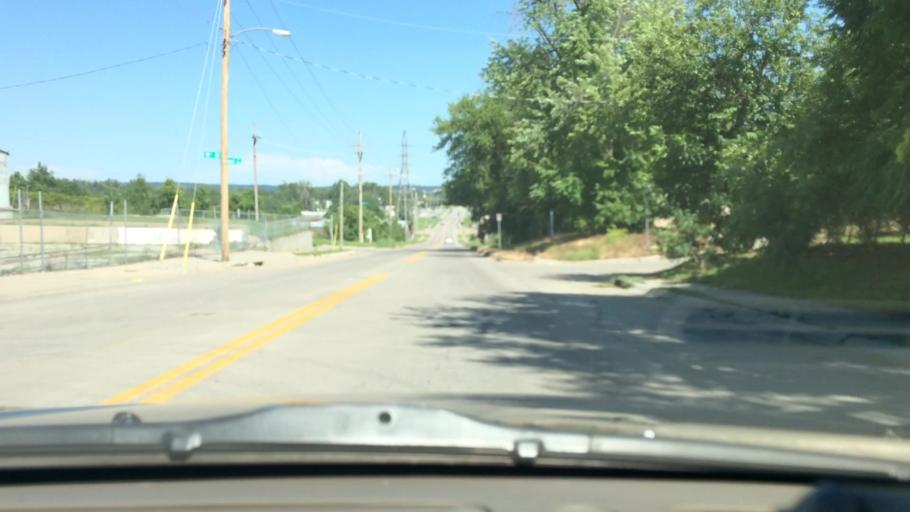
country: US
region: Iowa
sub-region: Pottawattamie County
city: Carter Lake
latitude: 41.2851
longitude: -95.9362
